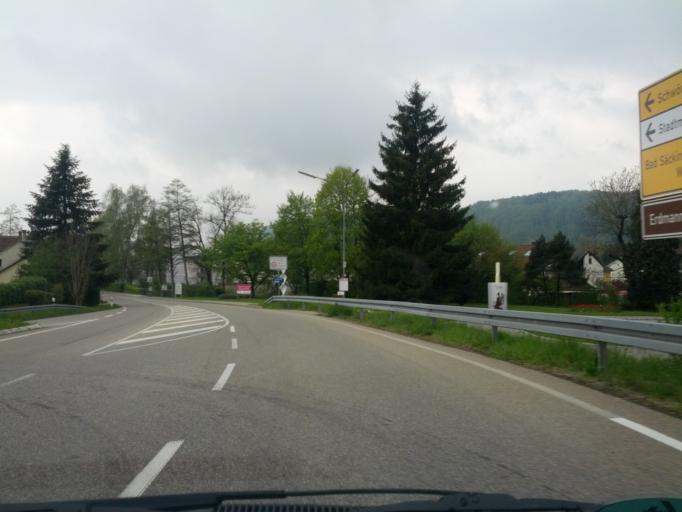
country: DE
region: Baden-Wuerttemberg
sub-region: Freiburg Region
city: Schopfheim
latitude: 47.6499
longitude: 7.8346
